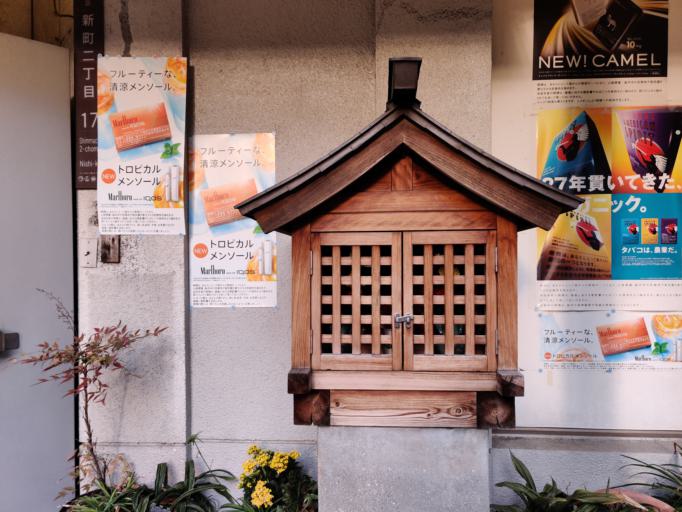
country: JP
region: Osaka
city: Osaka-shi
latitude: 34.6773
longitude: 135.4907
